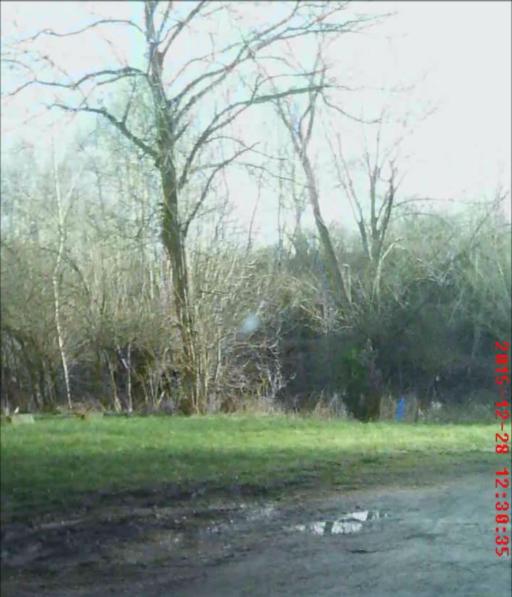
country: DE
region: Thuringia
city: Ossmanstedt
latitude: 51.0201
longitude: 11.4378
